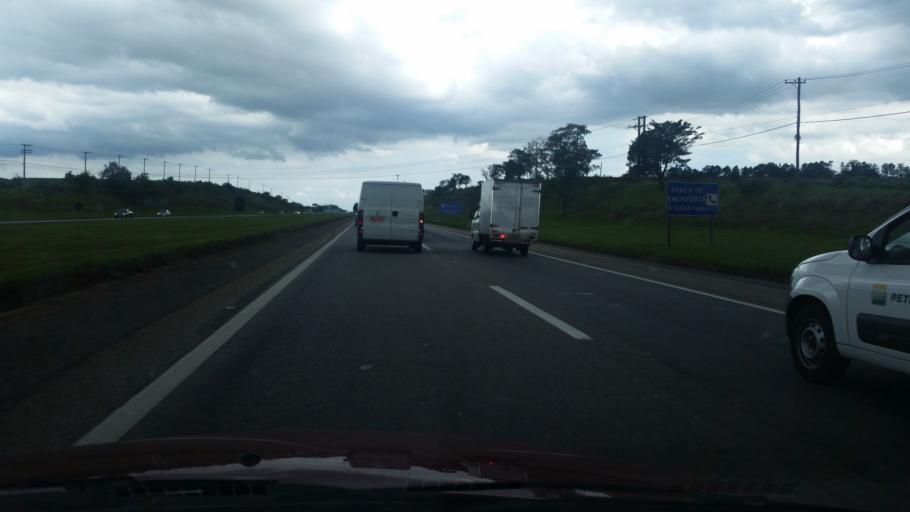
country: BR
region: Sao Paulo
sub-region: Porto Feliz
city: Porto Feliz
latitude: -23.3473
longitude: -47.5233
